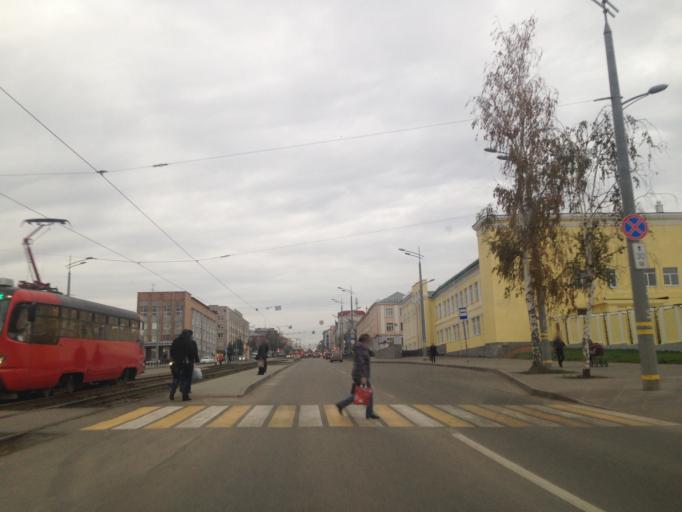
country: RU
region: Udmurtiya
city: Izhevsk
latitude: 56.8402
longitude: 53.2053
